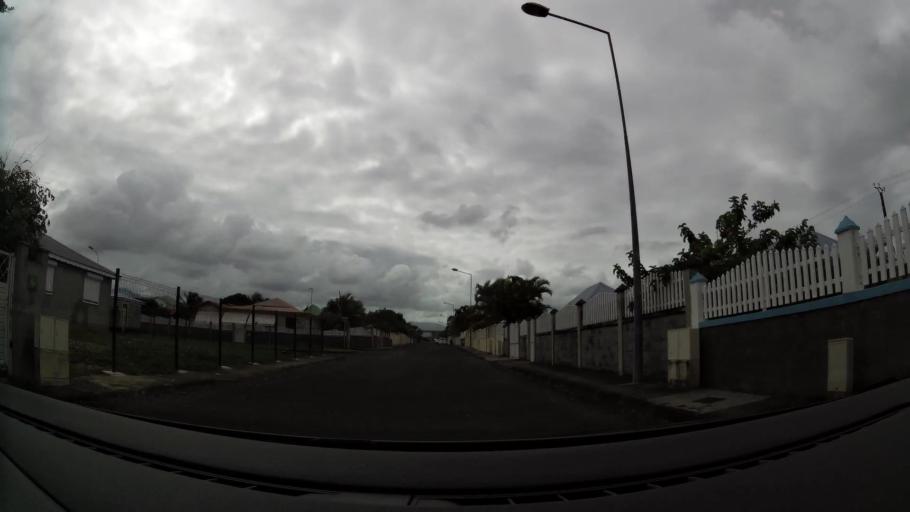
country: GP
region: Guadeloupe
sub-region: Guadeloupe
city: Lamentin
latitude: 16.2626
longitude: -61.6253
